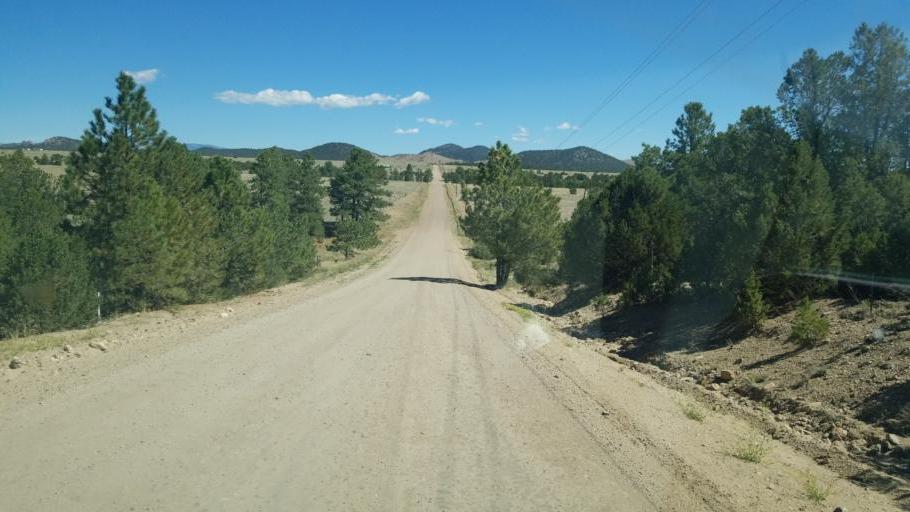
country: US
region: Colorado
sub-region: Custer County
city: Westcliffe
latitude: 38.2706
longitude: -105.5010
